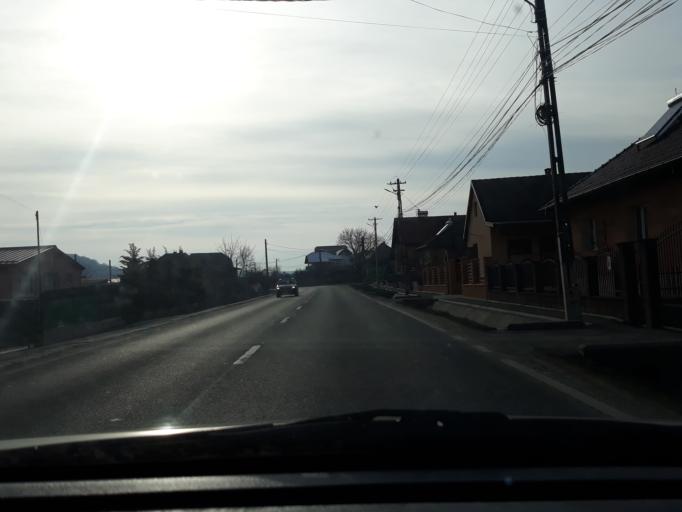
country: RO
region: Salaj
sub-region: Comuna Hereclean
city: Hereclean
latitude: 47.2396
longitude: 22.9893
